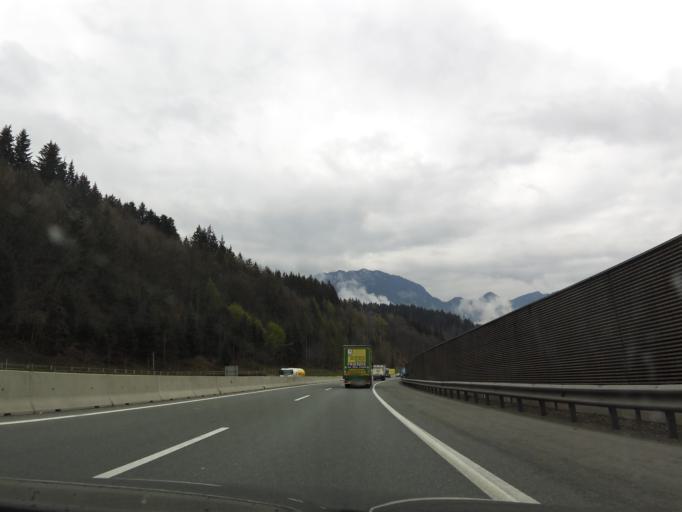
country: AT
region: Tyrol
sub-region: Politischer Bezirk Kufstein
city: Angath
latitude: 47.5013
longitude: 12.0581
